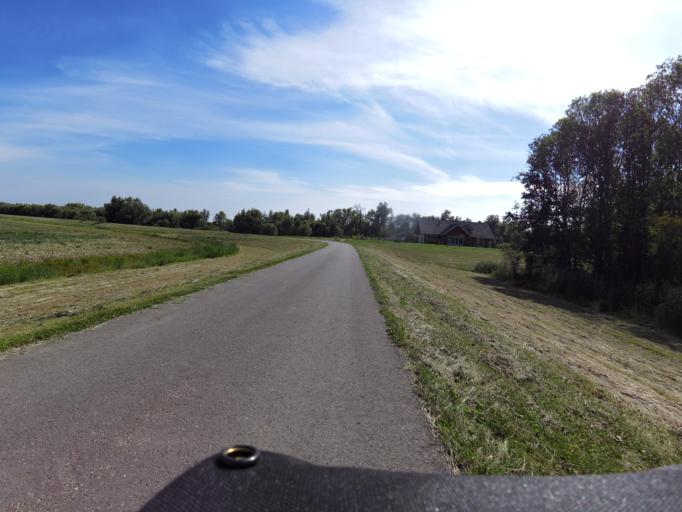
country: NL
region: North Brabant
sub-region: Gemeente Geertruidenberg
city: Geertruidenberg
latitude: 51.7627
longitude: 4.8391
